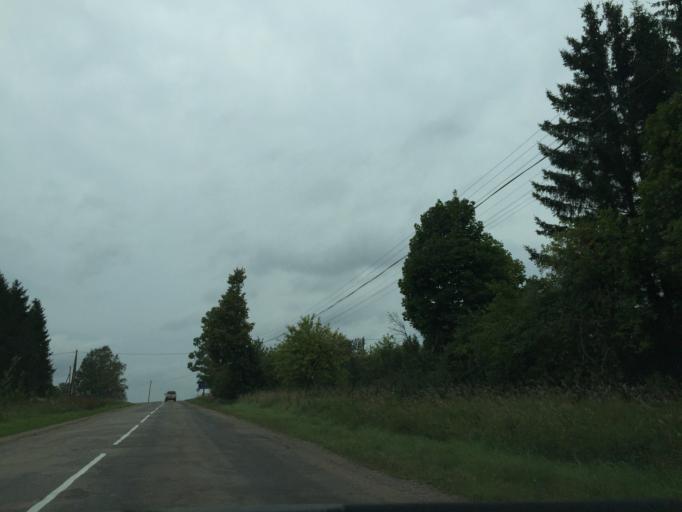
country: LV
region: Zilupes
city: Zilupe
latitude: 56.3867
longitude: 28.0901
